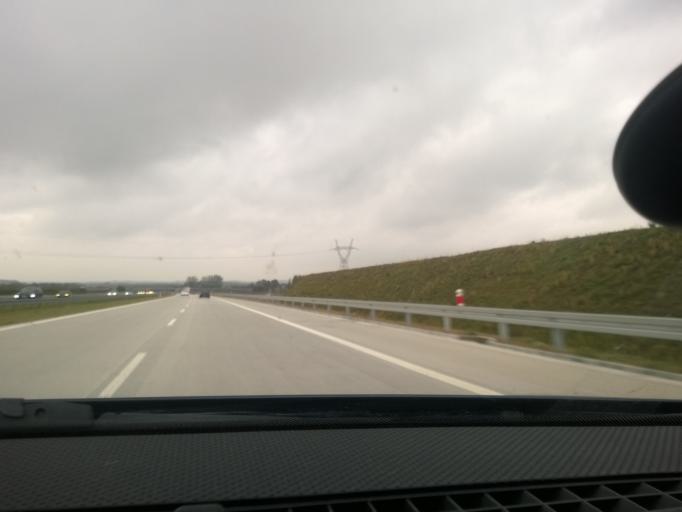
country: PL
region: Lodz Voivodeship
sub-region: Powiat zgierski
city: Strykow
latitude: 51.8595
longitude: 19.6589
